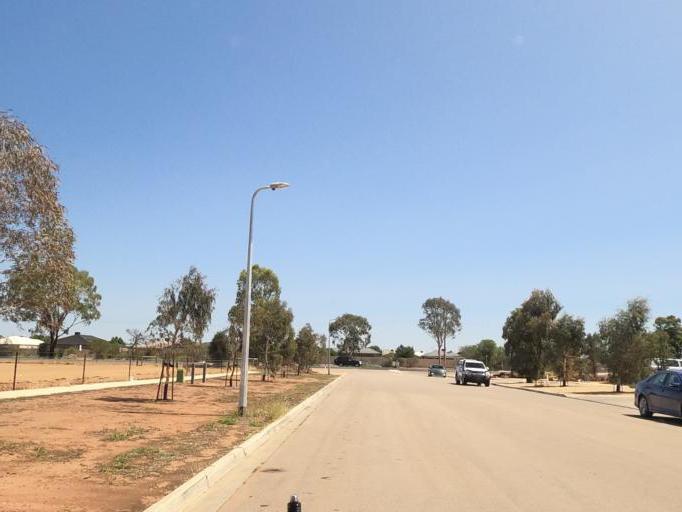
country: AU
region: Victoria
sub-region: Moira
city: Yarrawonga
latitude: -36.0124
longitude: 146.0252
